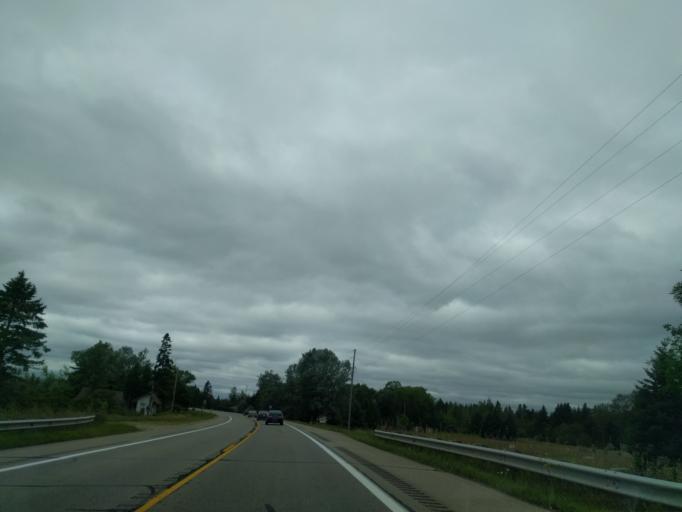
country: US
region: Michigan
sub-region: Delta County
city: Escanaba
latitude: 45.6412
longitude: -87.1946
